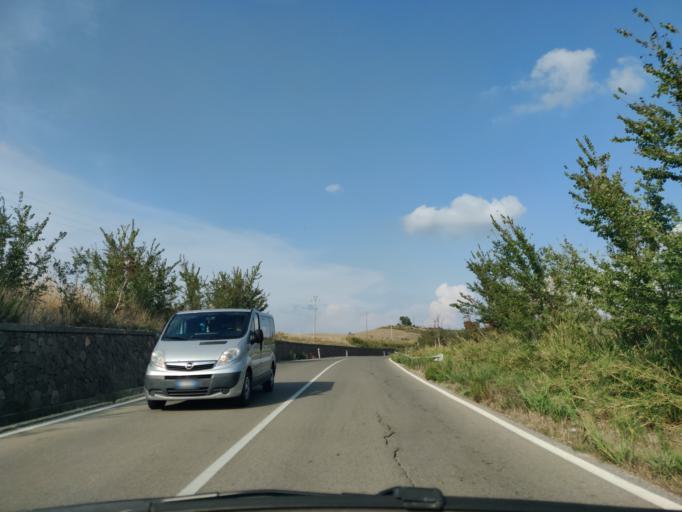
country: IT
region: Latium
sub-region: Provincia di Viterbo
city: Tarquinia
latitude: 42.2574
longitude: 11.8187
